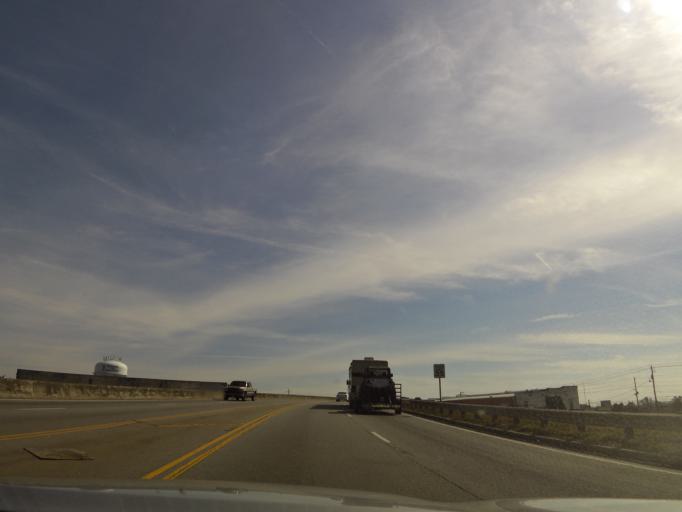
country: US
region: Georgia
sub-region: Ware County
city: Waycross
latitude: 31.2085
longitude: -82.3627
